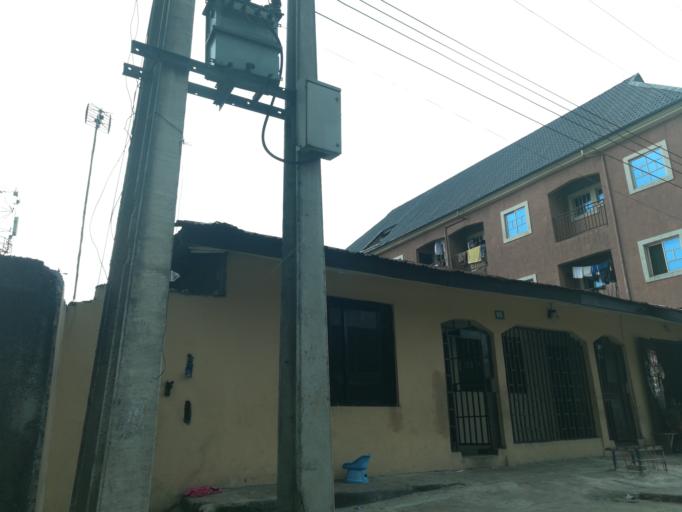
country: NG
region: Rivers
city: Port Harcourt
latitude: 4.7927
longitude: 6.9853
